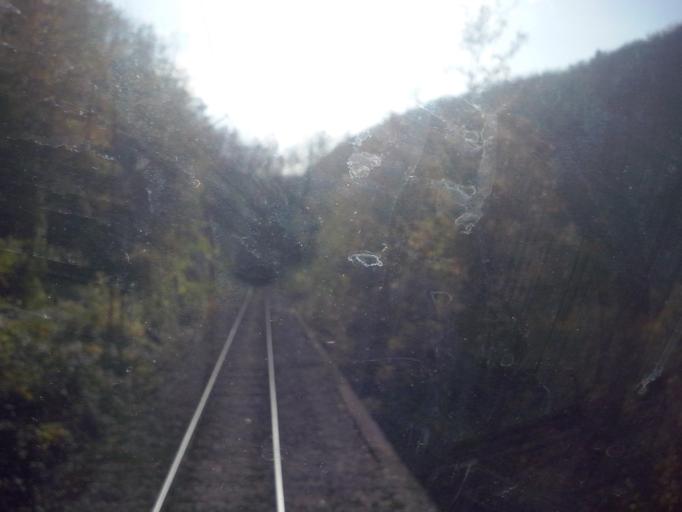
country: RS
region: Central Serbia
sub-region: Kolubarski Okrug
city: Valjevo
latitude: 44.1915
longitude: 19.8640
